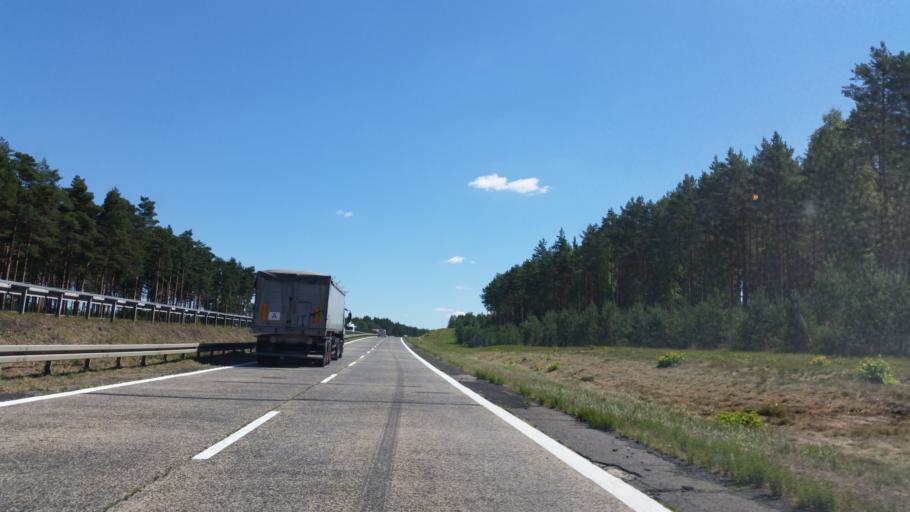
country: PL
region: Lubusz
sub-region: Powiat zaganski
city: Malomice
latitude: 51.4200
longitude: 15.4706
